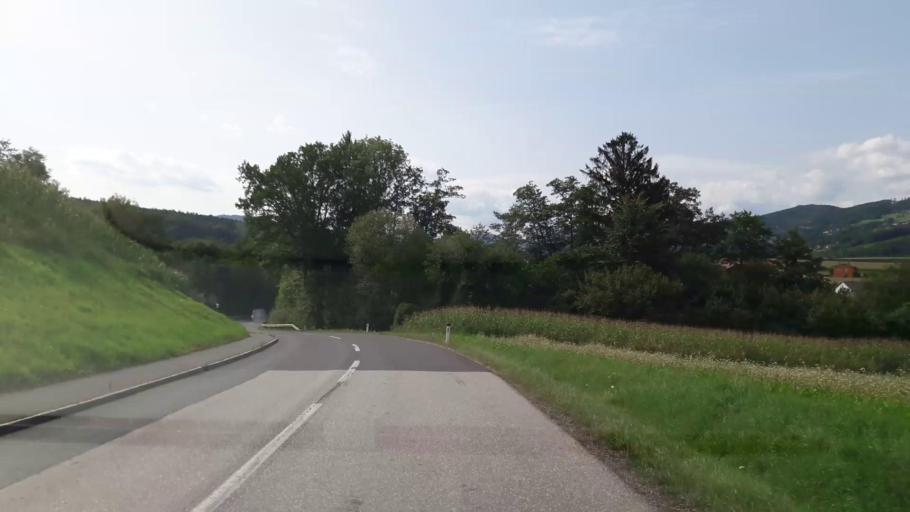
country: AT
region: Styria
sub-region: Politischer Bezirk Hartberg-Fuerstenfeld
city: Dienersdorf
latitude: 47.2214
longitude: 15.8603
